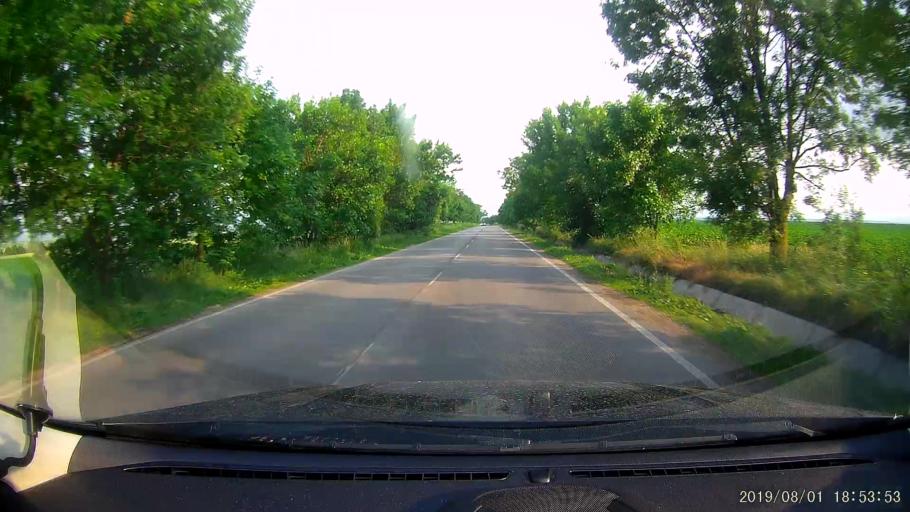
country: BG
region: Shumen
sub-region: Obshtina Shumen
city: Shumen
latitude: 43.2125
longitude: 26.9982
